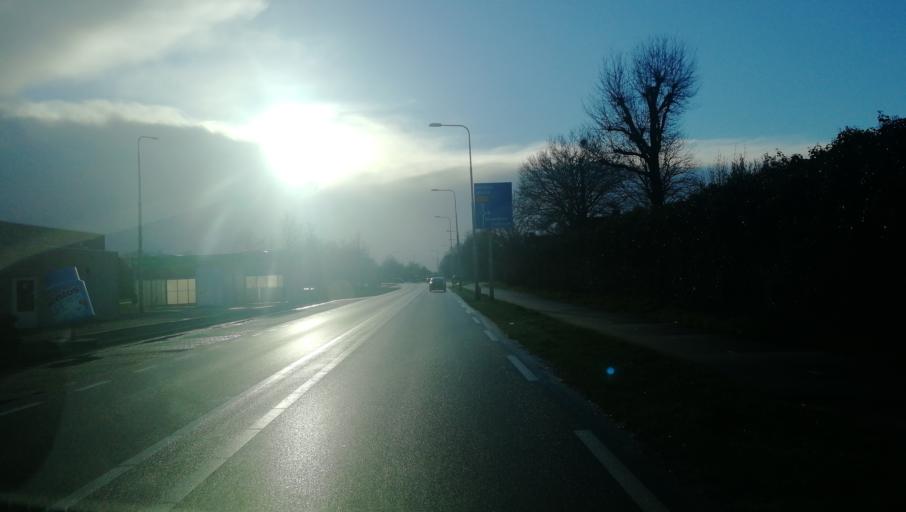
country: NL
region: Limburg
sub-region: Gemeente Peel en Maas
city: Maasbree
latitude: 51.3550
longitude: 6.0490
